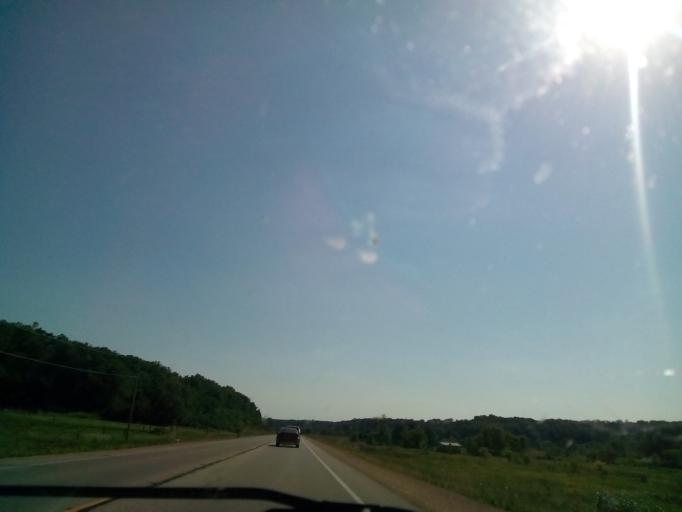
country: US
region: Wisconsin
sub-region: Green County
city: New Glarus
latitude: 42.8539
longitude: -89.6236
